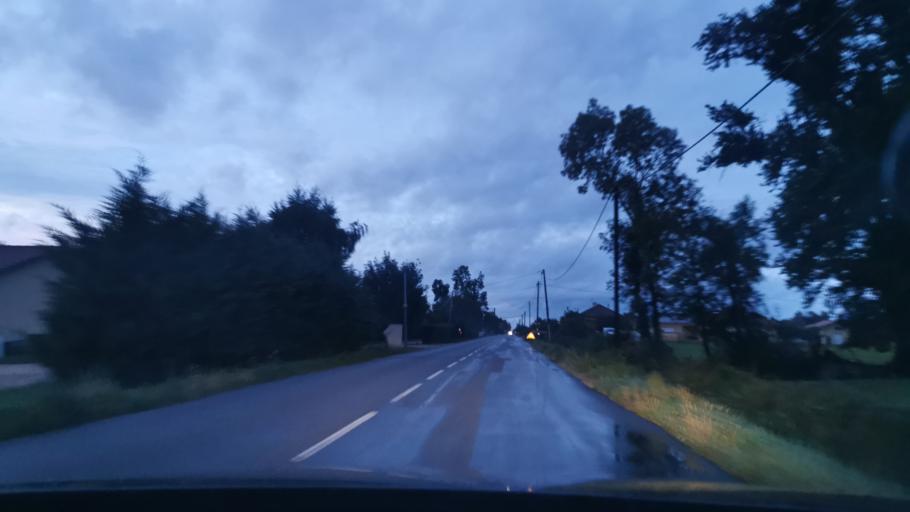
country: FR
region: Rhone-Alpes
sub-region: Departement de l'Ain
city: Bage-la-Ville
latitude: 46.3252
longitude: 4.9350
